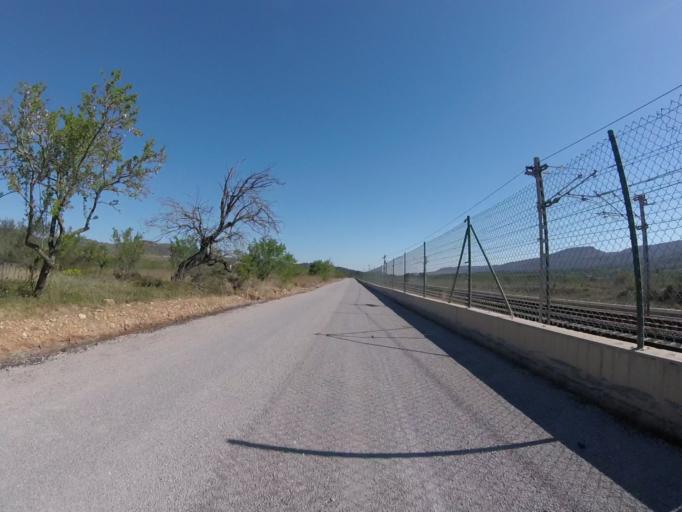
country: ES
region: Valencia
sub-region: Provincia de Castello
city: Alcala de Xivert
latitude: 40.3364
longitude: 0.2555
